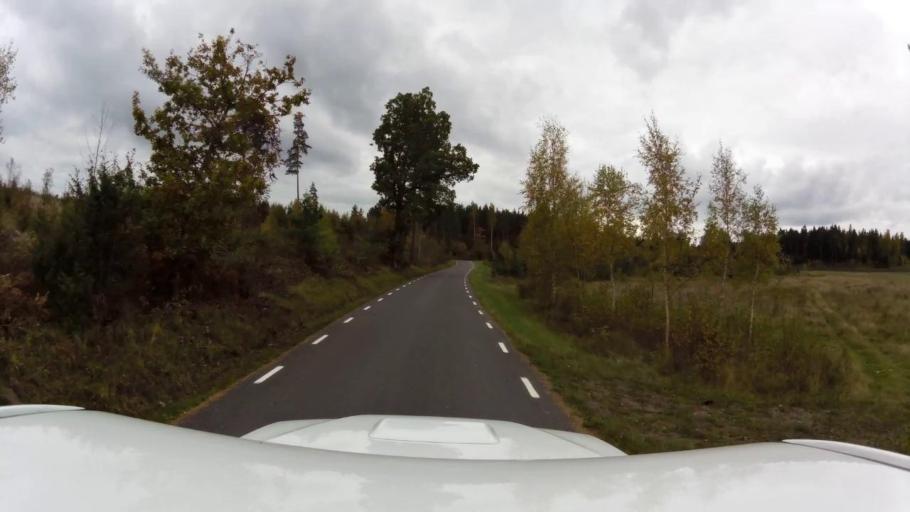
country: SE
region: OEstergoetland
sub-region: Linkopings Kommun
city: Ljungsbro
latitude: 58.5420
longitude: 15.4475
